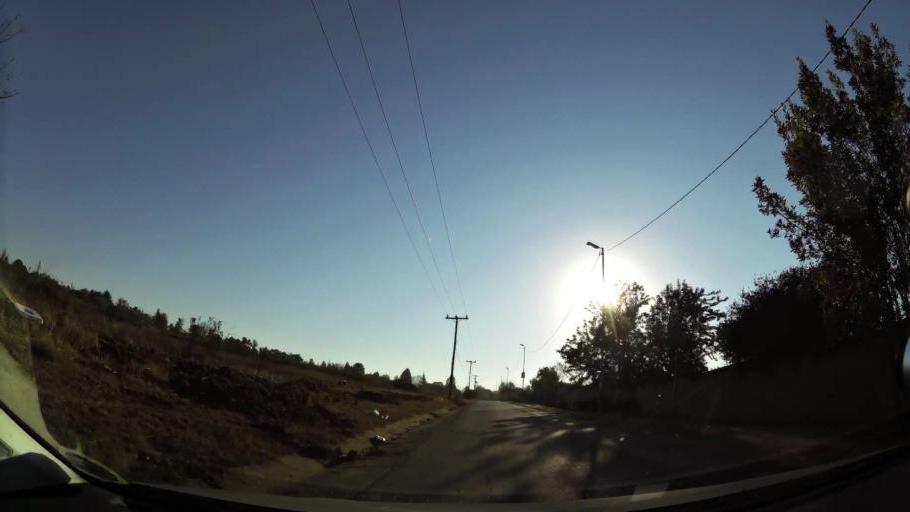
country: ZA
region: Gauteng
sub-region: City of Johannesburg Metropolitan Municipality
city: Midrand
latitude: -26.0172
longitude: 28.1366
